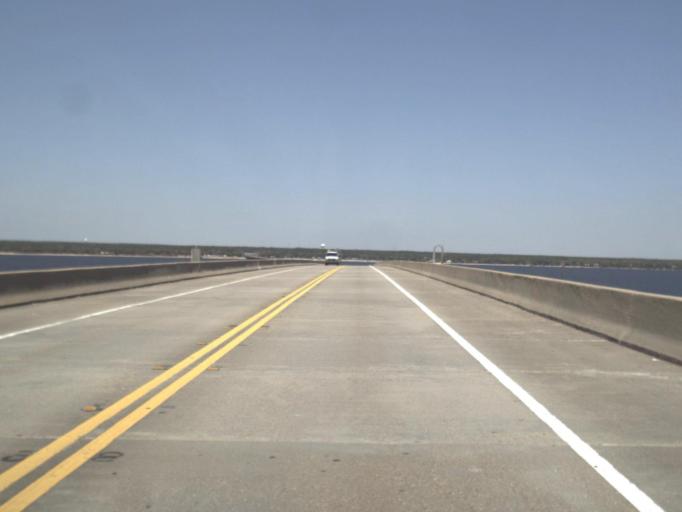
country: US
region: Florida
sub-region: Walton County
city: Miramar Beach
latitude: 30.4329
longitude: -86.4180
